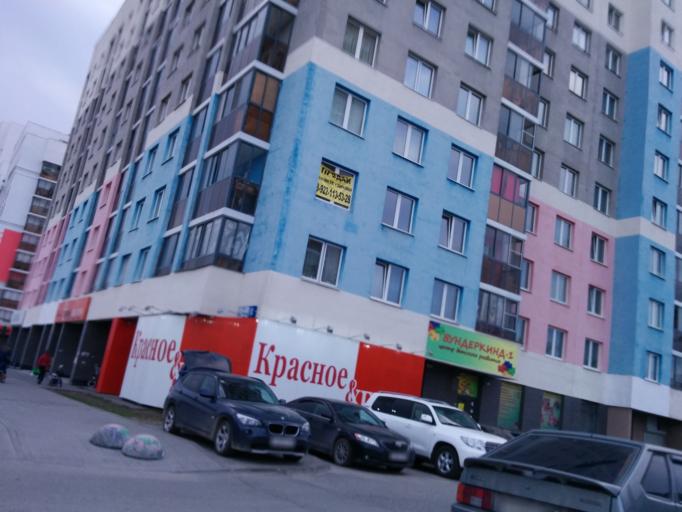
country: RU
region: Sverdlovsk
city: Shirokaya Rechka
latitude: 56.7927
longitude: 60.5097
